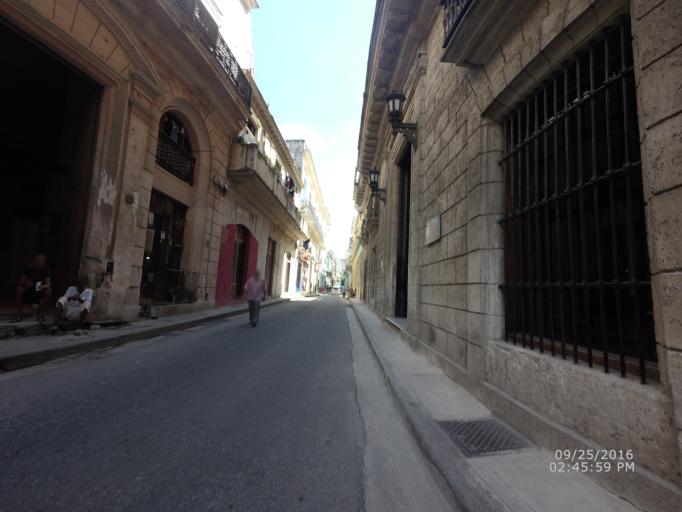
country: CU
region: La Habana
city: Centro Habana
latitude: 23.1418
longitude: -82.3534
